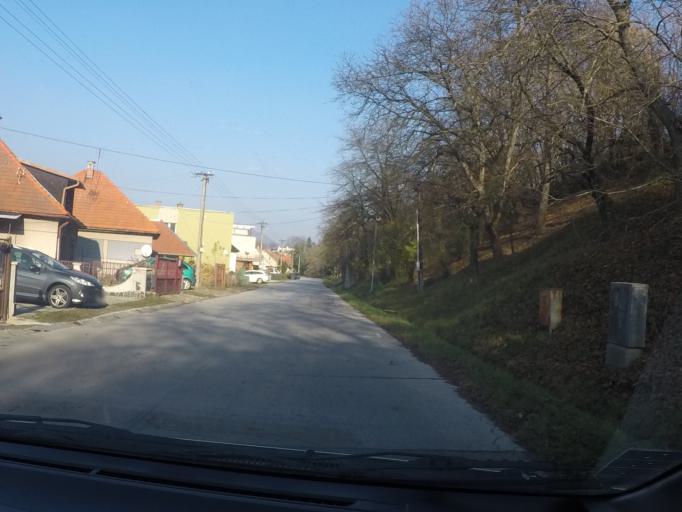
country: SK
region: Banskobystricky
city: Nova Bana
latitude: 48.3806
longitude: 18.6137
